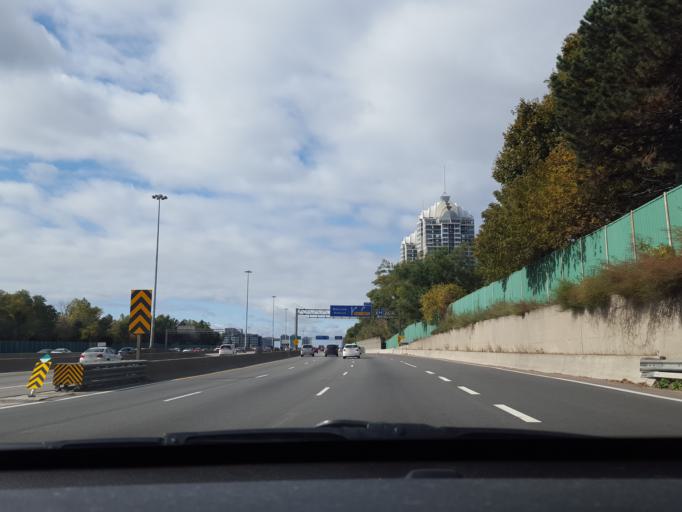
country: CA
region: Ontario
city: Willowdale
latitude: 43.7657
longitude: -79.3771
